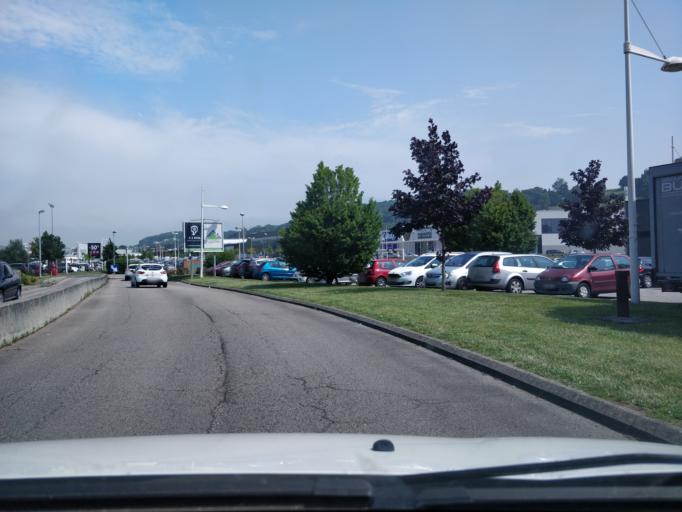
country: FR
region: Haute-Normandie
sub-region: Departement de la Seine-Maritime
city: Harfleur
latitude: 49.5227
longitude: 0.1906
